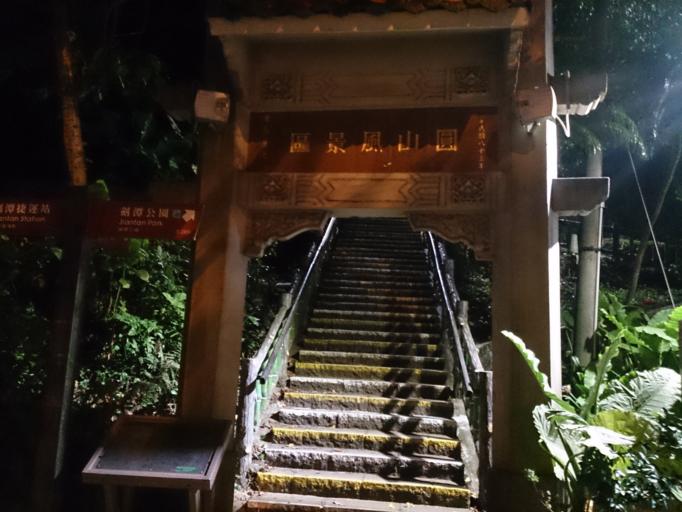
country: TW
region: Taipei
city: Taipei
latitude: 25.0809
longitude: 121.5246
